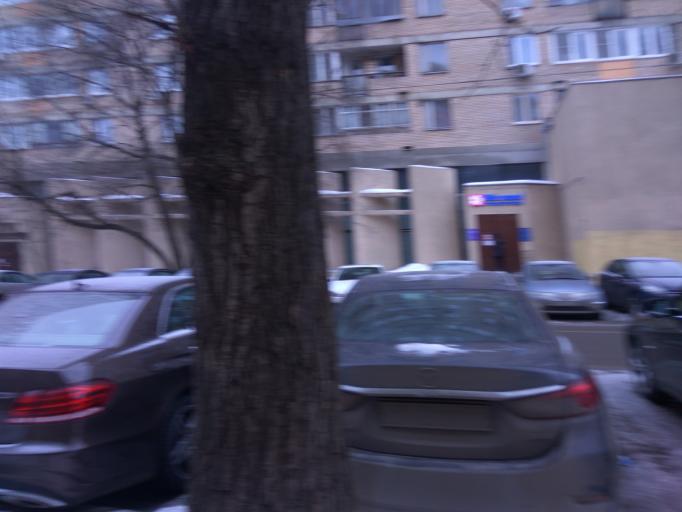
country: RU
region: Moscow
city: Taganskiy
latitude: 55.7302
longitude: 37.6648
